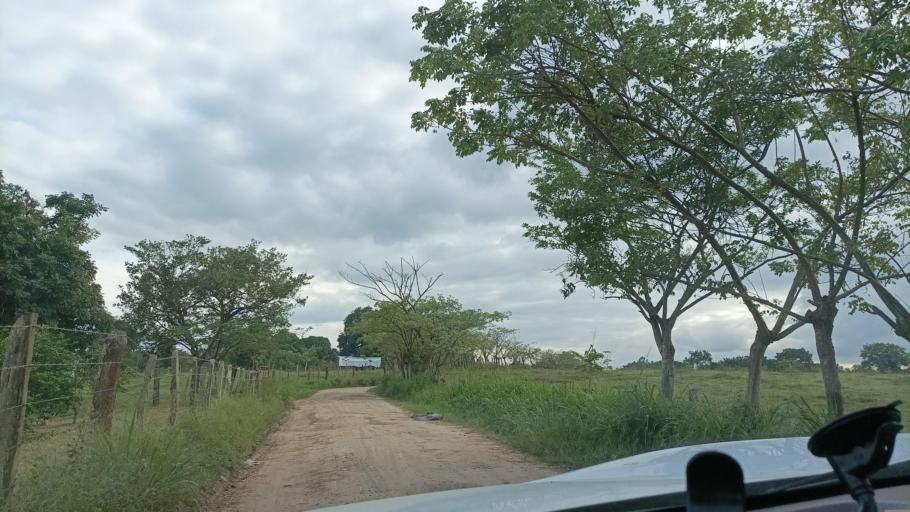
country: MX
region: Veracruz
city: Oluta
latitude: 17.9284
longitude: -94.8838
